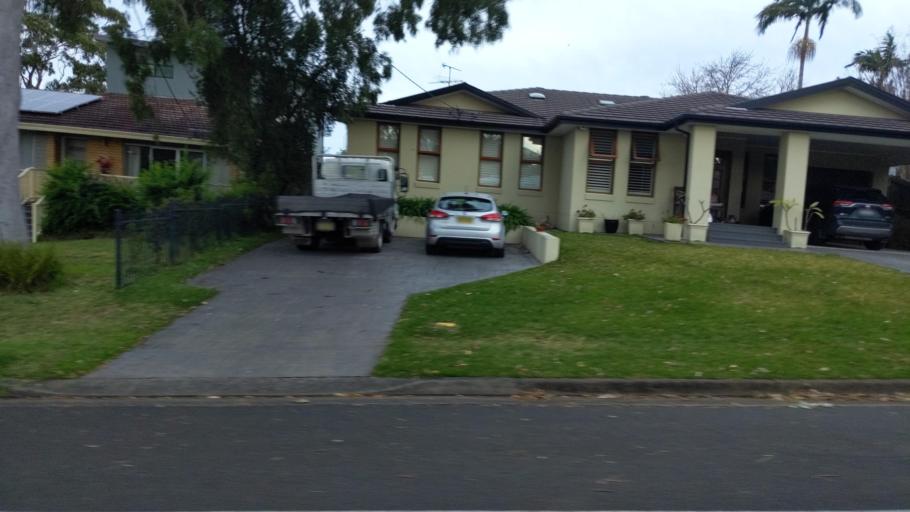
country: AU
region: New South Wales
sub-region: The Hills Shire
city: Baulkham Hills
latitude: -33.7487
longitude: 150.9646
